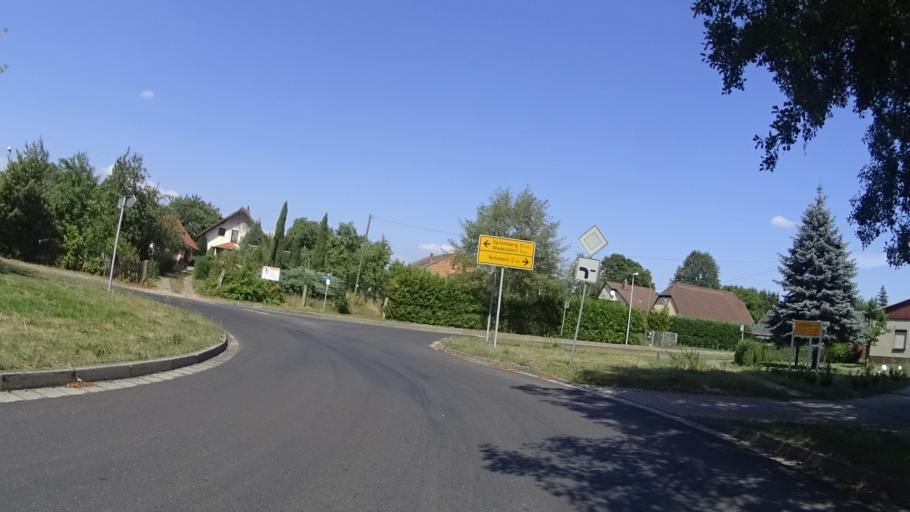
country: DE
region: Saxony
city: Gross Duben
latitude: 51.6081
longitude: 14.5065
